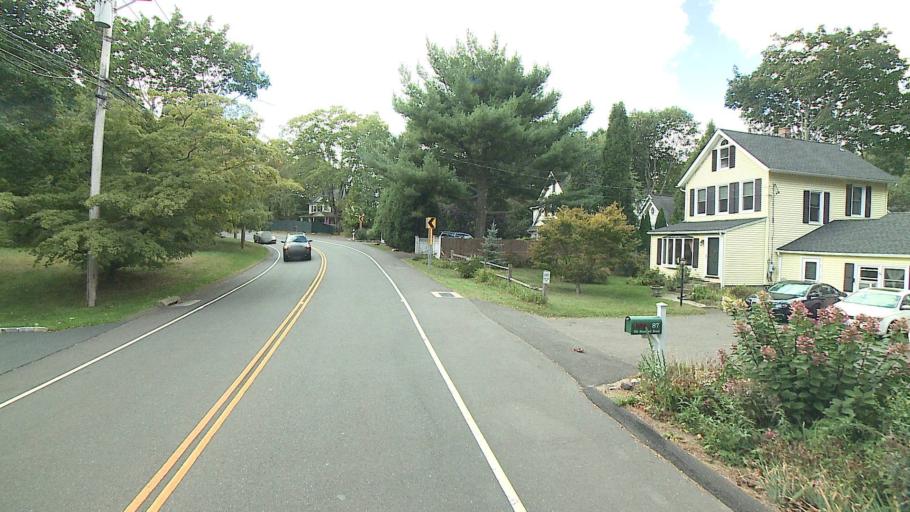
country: US
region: Connecticut
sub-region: Fairfield County
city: New Canaan
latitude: 41.1354
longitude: -73.4964
